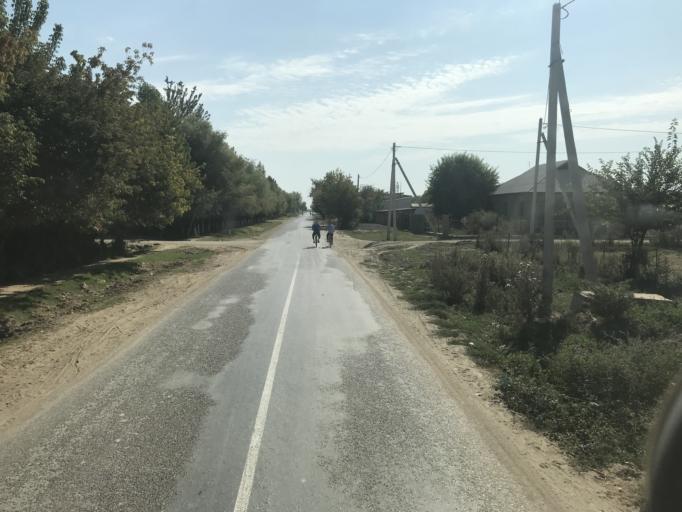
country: KZ
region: Ongtustik Qazaqstan
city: Myrzakent
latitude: 40.6643
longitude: 68.6202
